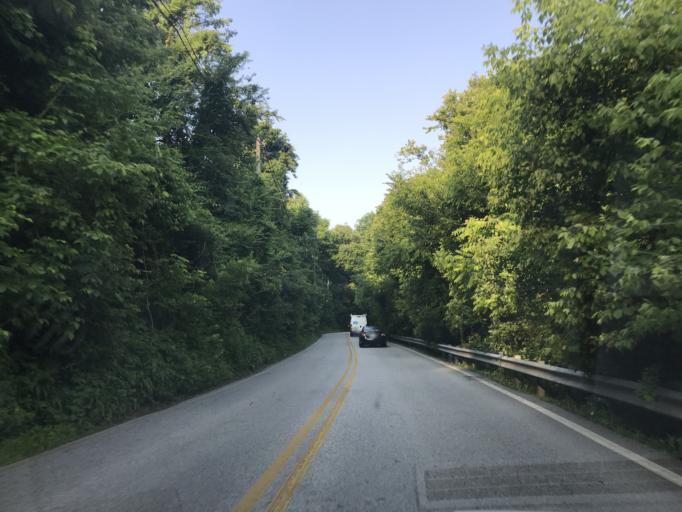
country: US
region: Maryland
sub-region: Baltimore County
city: Carney
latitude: 39.4246
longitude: -76.5306
